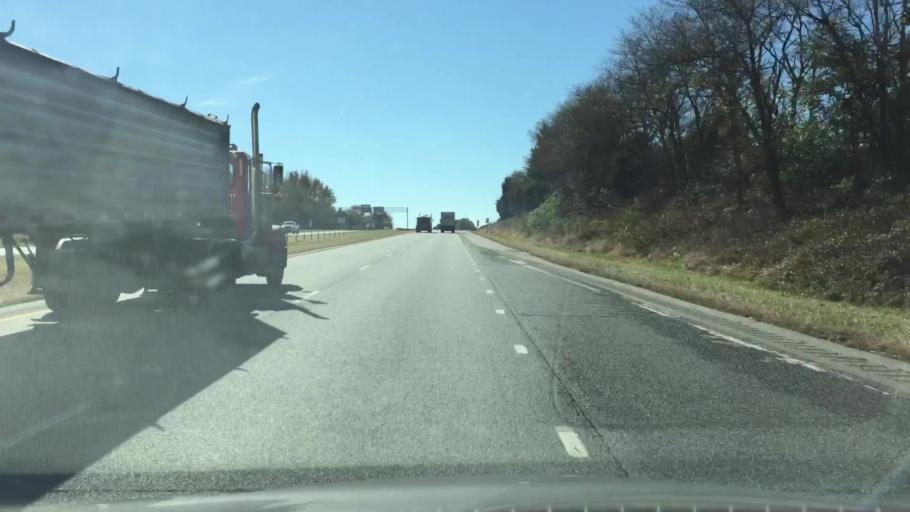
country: US
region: North Carolina
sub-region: Rockingham County
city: Reidsville
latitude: 36.2591
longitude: -79.6543
